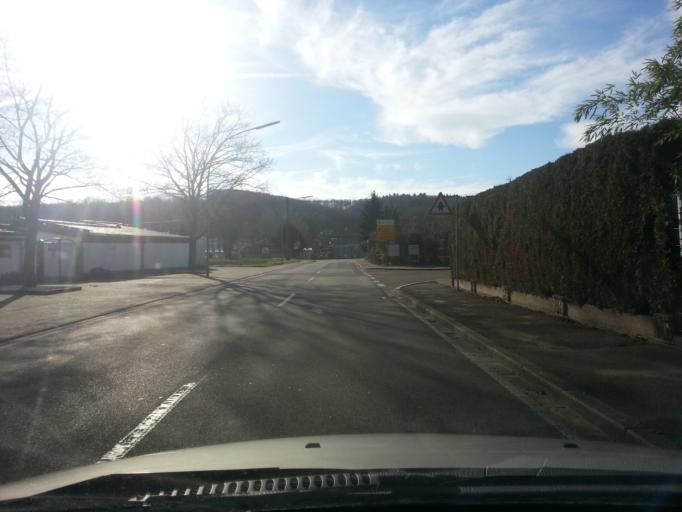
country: DE
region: Baden-Wuerttemberg
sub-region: Karlsruhe Region
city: Ostringen
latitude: 49.1837
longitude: 8.7371
